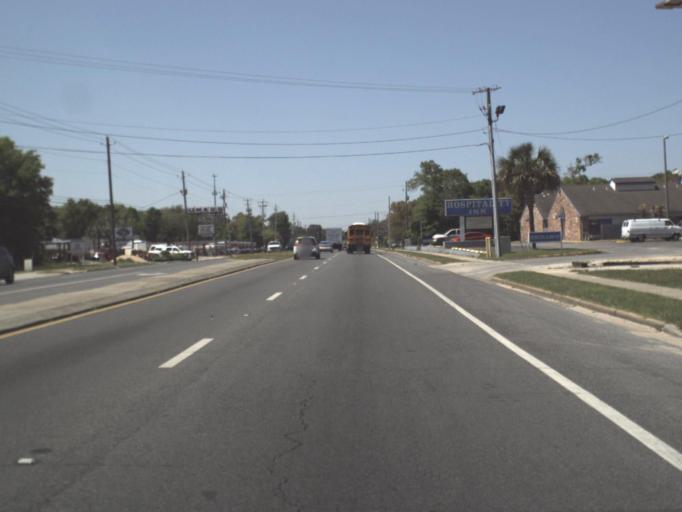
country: US
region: Florida
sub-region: Escambia County
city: West Pensacola
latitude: 30.4409
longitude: -87.2828
